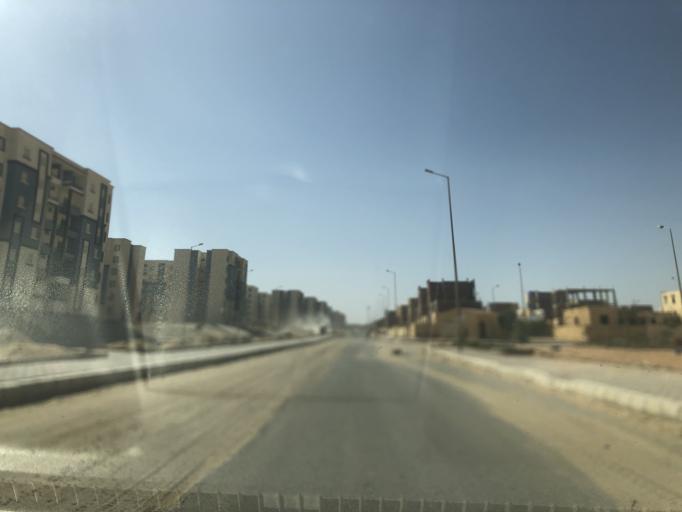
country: EG
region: Al Jizah
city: Madinat Sittah Uktubar
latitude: 29.9307
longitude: 30.9879
